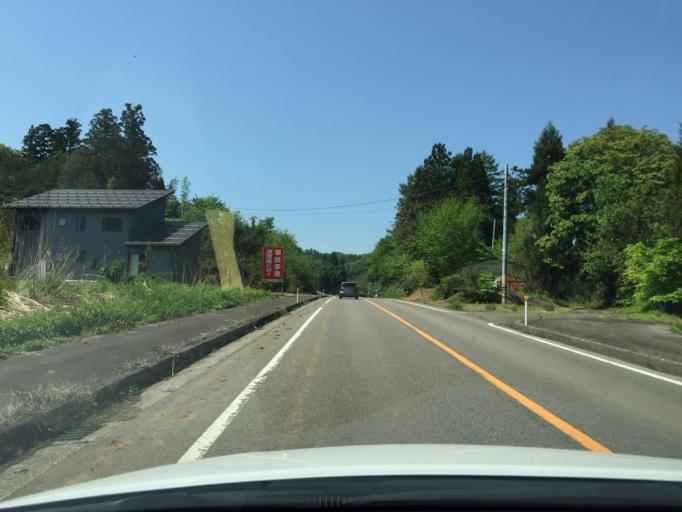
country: JP
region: Niigata
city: Muramatsu
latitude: 37.6457
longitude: 139.1267
